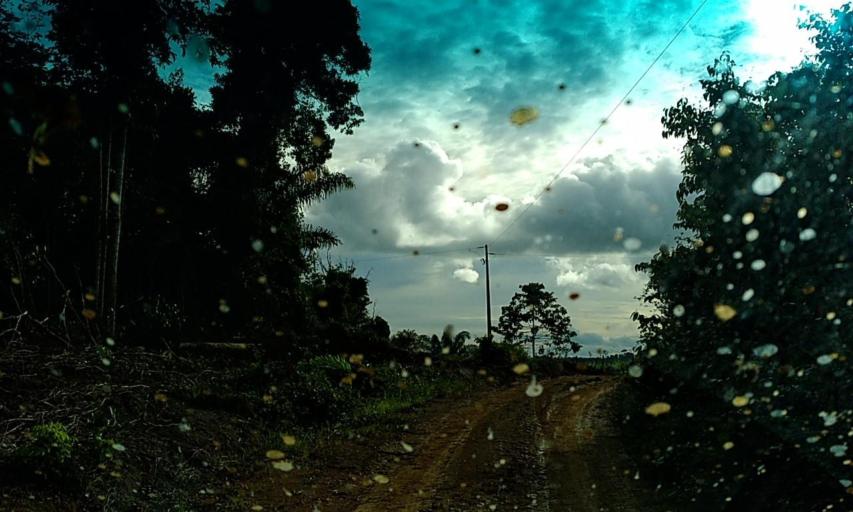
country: BR
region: Para
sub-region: Senador Jose Porfirio
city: Senador Jose Porfirio
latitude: -3.0089
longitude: -51.7467
